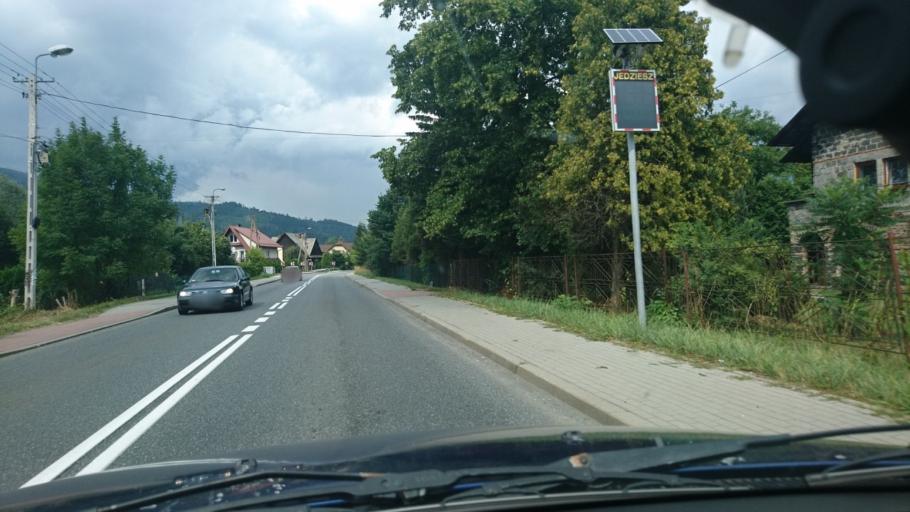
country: PL
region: Silesian Voivodeship
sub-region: Powiat zywiecki
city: Cisiec
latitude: 49.5974
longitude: 19.1075
